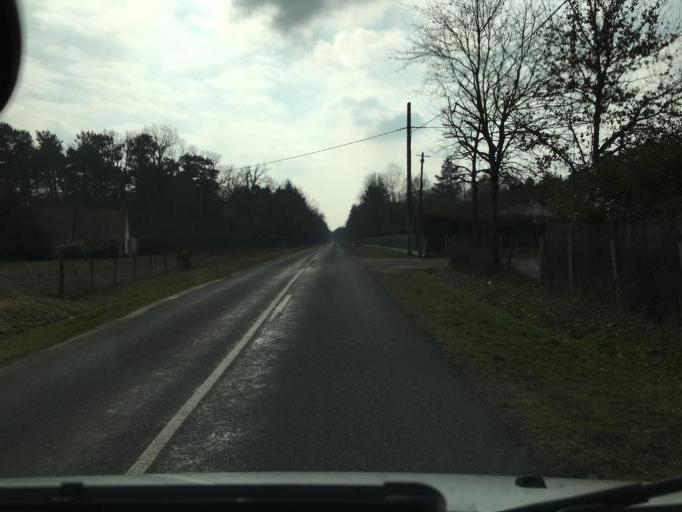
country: FR
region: Centre
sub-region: Departement du Loiret
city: Ligny-le-Ribault
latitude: 47.6171
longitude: 1.7507
